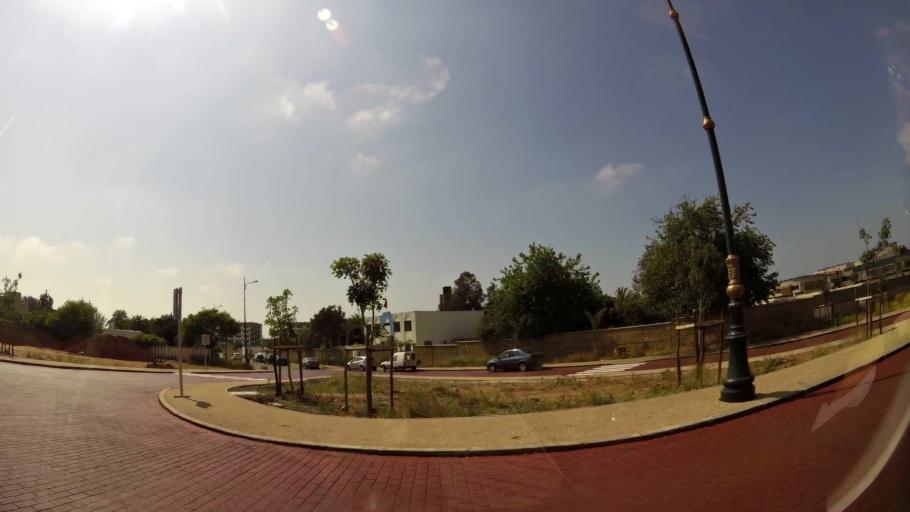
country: MA
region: Rabat-Sale-Zemmour-Zaer
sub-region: Rabat
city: Rabat
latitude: 33.9804
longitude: -6.8584
